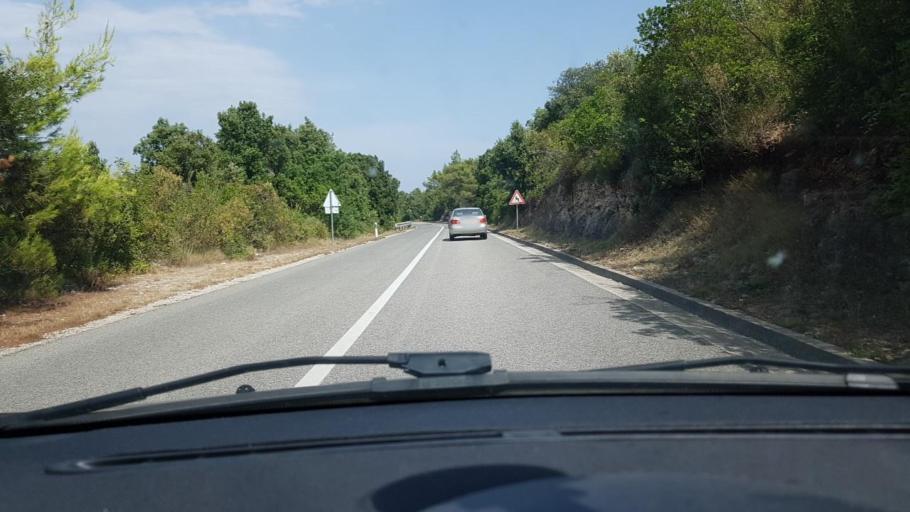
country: HR
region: Dubrovacko-Neretvanska
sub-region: Grad Korcula
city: Zrnovo
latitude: 42.9400
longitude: 17.0635
